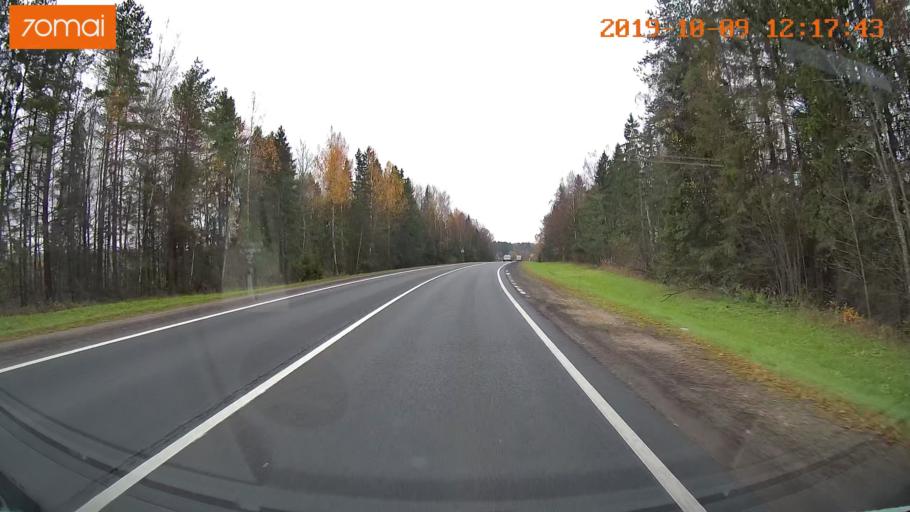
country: RU
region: Jaroslavl
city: Prechistoye
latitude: 58.4525
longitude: 40.3217
